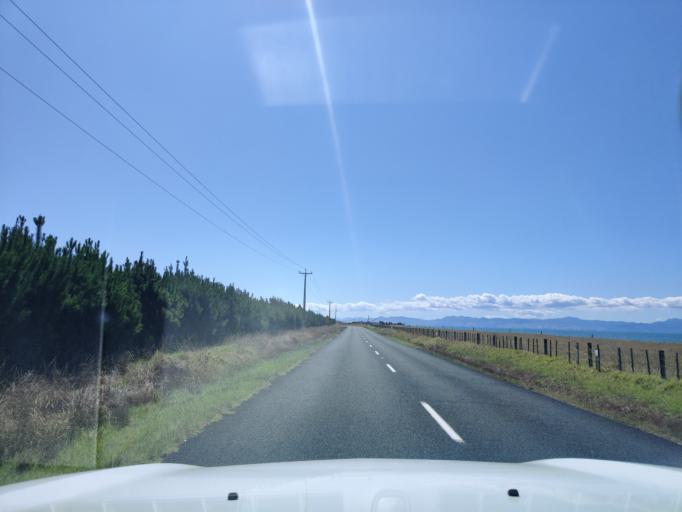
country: NZ
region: Waikato
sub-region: Thames-Coromandel District
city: Thames
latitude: -37.0666
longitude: 175.2970
